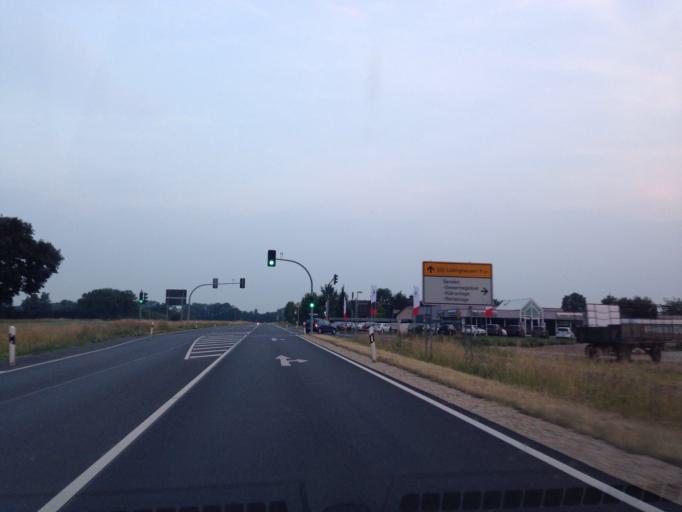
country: DE
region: North Rhine-Westphalia
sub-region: Regierungsbezirk Munster
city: Senden
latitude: 51.8477
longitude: 7.4885
